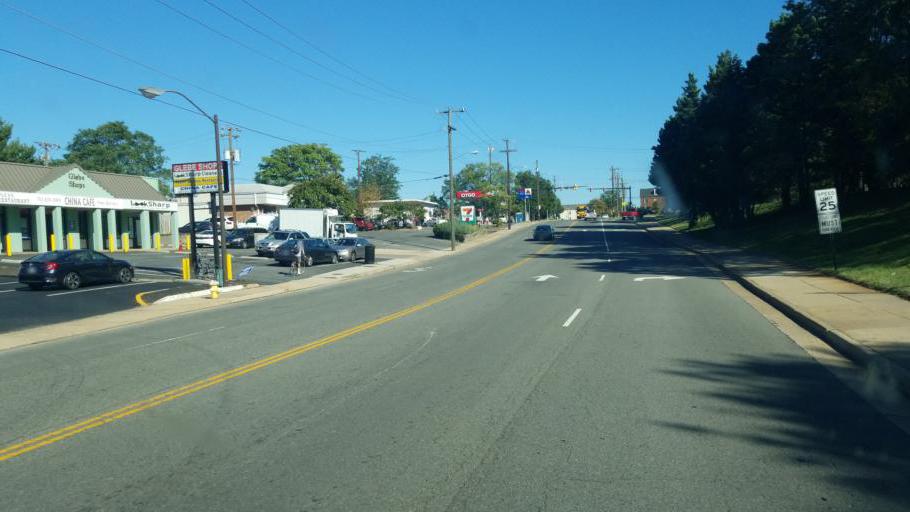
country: US
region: Virginia
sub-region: Arlington County
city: Arlington
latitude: 38.8428
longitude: -77.0765
